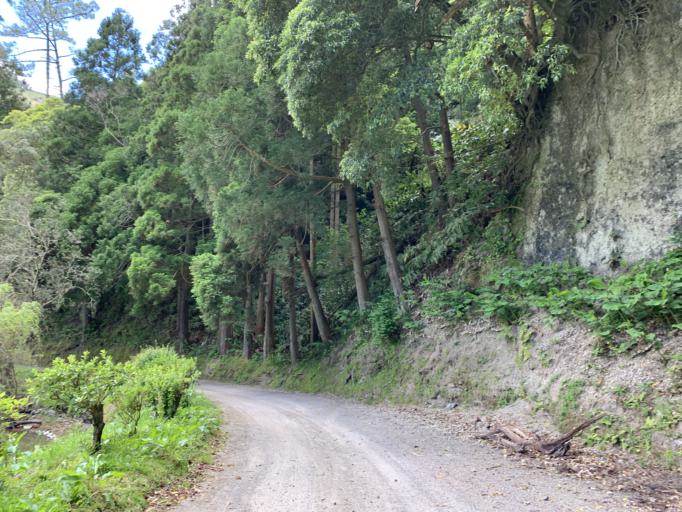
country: PT
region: Azores
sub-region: Ponta Delgada
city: Arrifes
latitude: 37.8453
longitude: -25.7946
